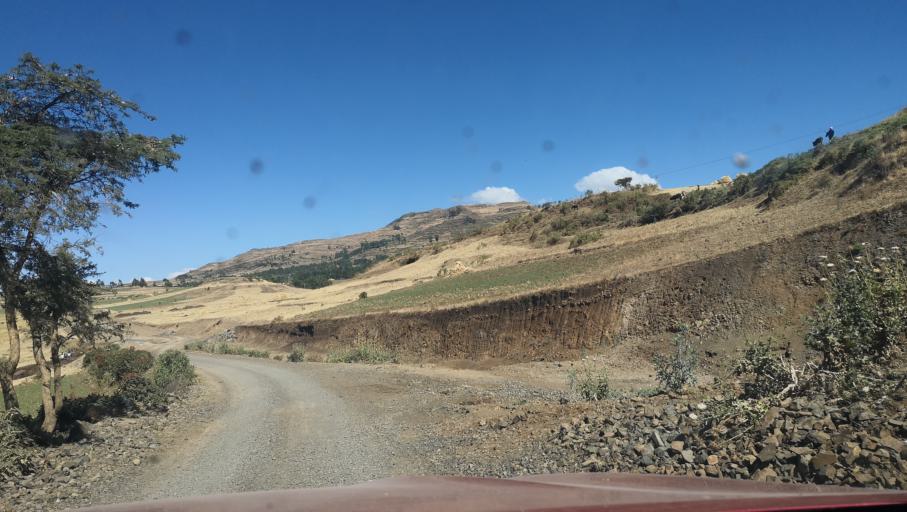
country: ET
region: Amhara
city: Debre Tabor
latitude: 11.5597
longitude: 38.1408
